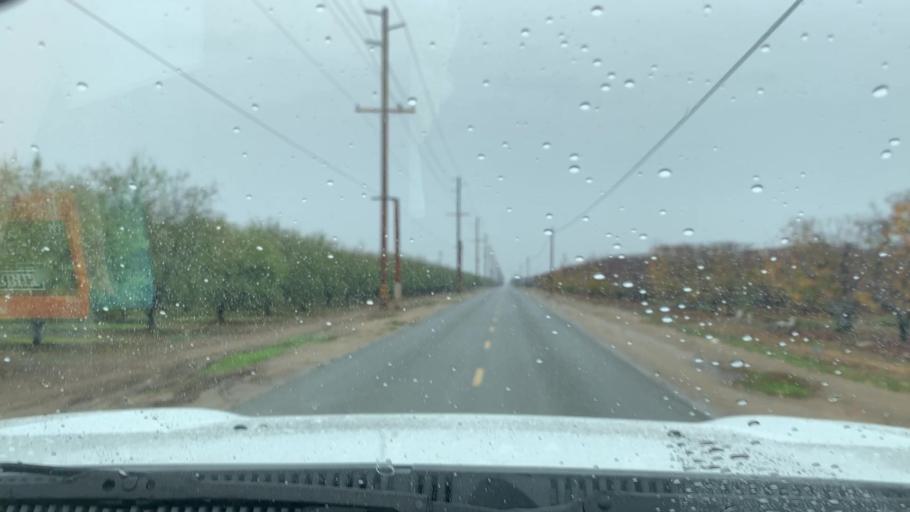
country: US
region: California
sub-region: Kern County
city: Delano
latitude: 35.8341
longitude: -119.1996
